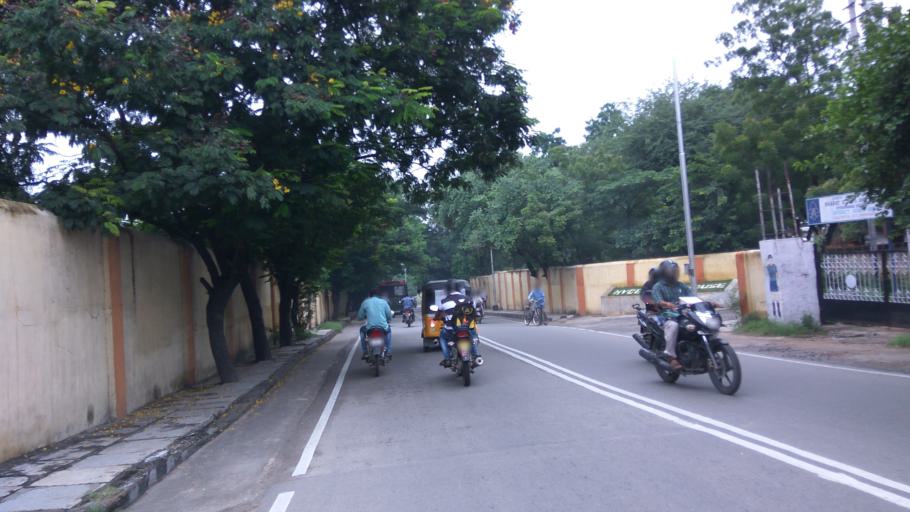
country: IN
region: Telangana
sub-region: Hyderabad
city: Malkajgiri
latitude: 17.4359
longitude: 78.5219
